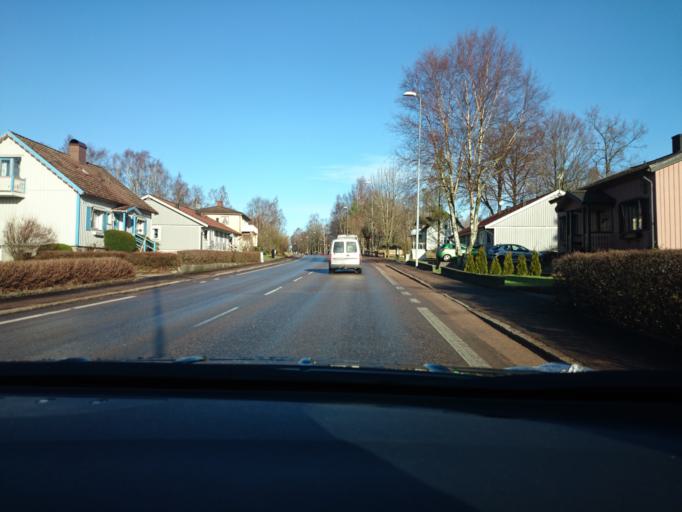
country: SE
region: Halland
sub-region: Hylte Kommun
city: Hyltebruk
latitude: 57.0094
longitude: 13.2425
